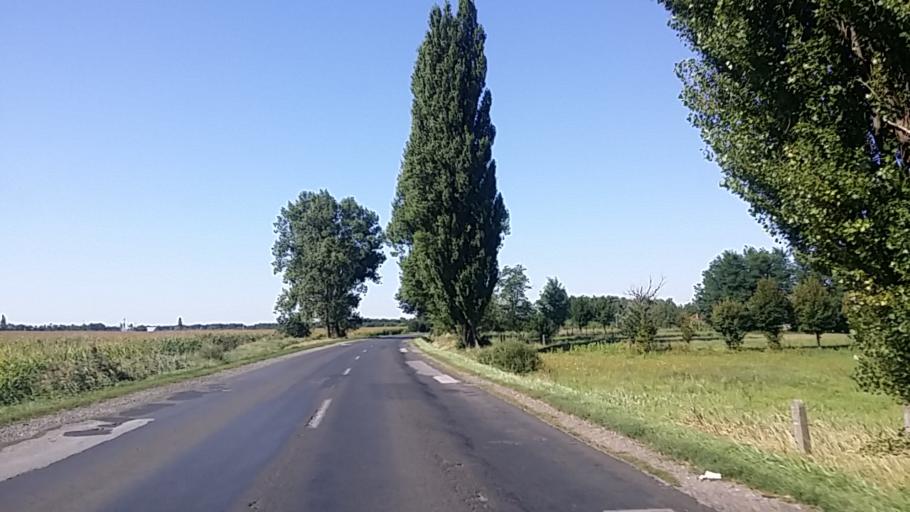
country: HU
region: Fejer
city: Mezofalva
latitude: 46.9341
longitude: 18.7969
